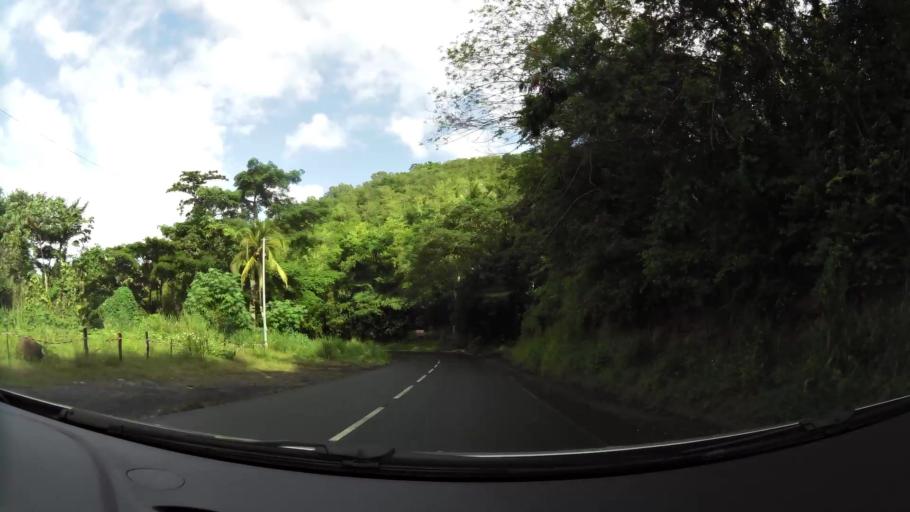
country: MQ
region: Martinique
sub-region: Martinique
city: Les Trois-Ilets
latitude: 14.5376
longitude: -61.0549
